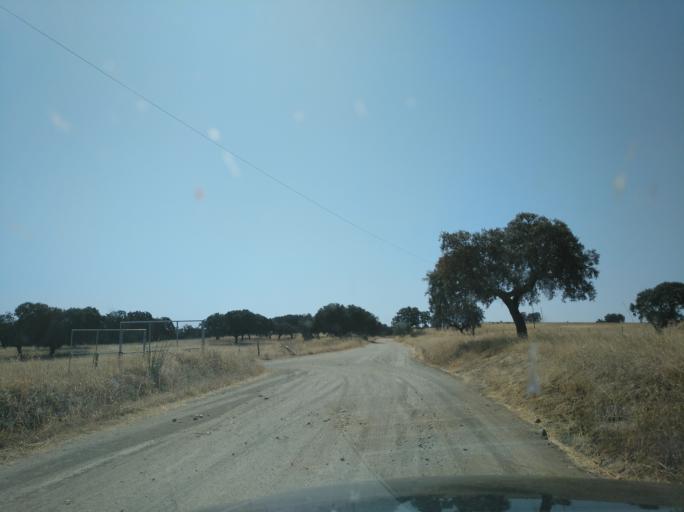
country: PT
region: Portalegre
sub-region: Campo Maior
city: Campo Maior
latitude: 39.0282
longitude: -6.9778
